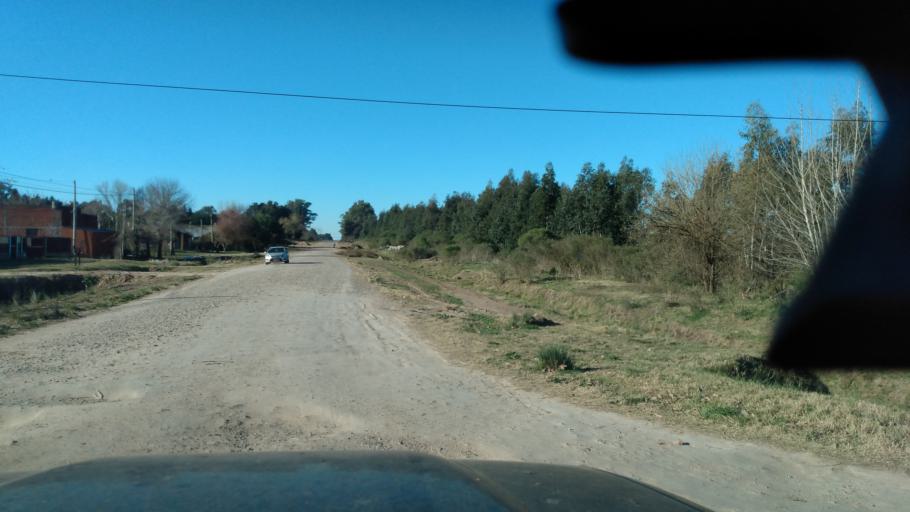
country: AR
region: Buenos Aires
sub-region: Partido de Lujan
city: Lujan
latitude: -34.5691
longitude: -59.1774
